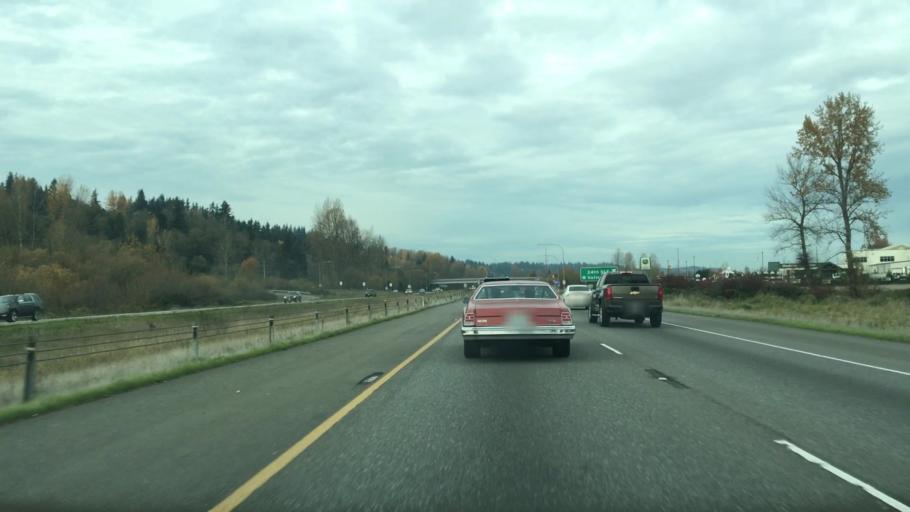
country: US
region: Washington
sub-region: Pierce County
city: Sumner
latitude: 47.2303
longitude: -122.2493
